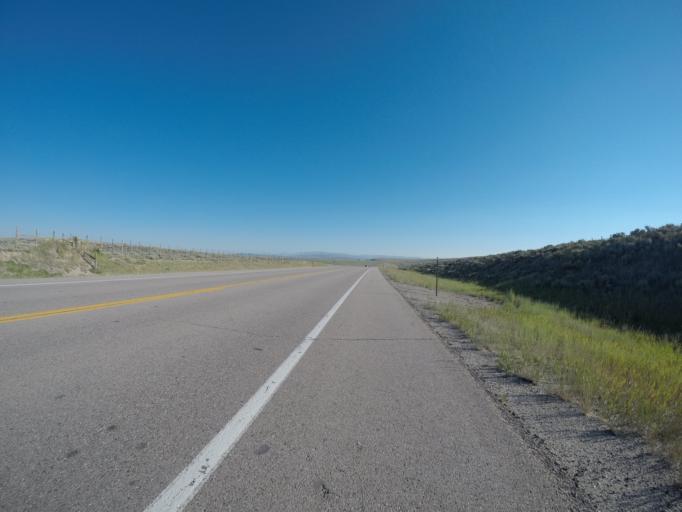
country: US
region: Wyoming
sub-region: Sublette County
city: Pinedale
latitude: 42.9219
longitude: -110.0805
